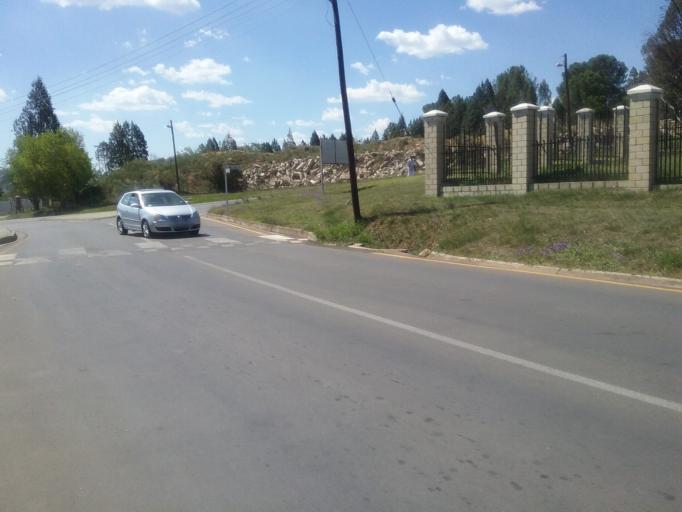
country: LS
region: Maseru
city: Maseru
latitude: -29.3068
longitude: 27.4740
